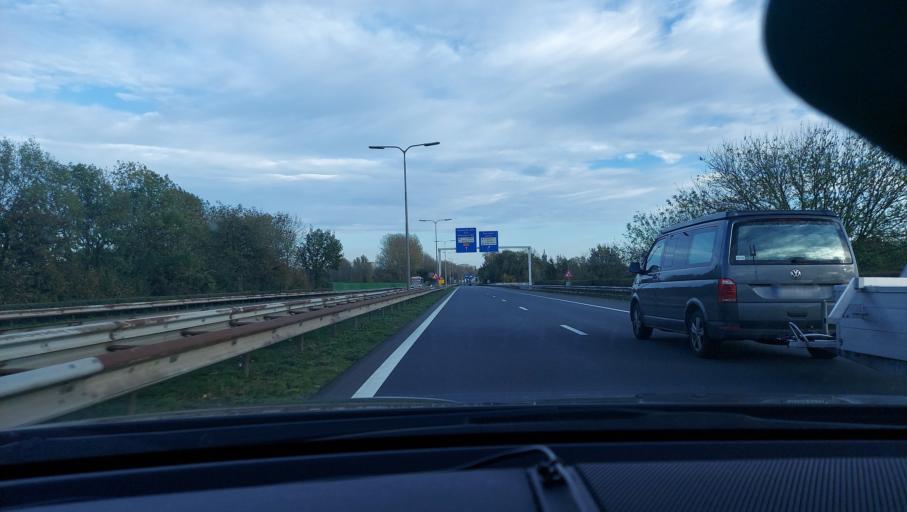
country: NL
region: Limburg
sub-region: Gemeente Roermond
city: Roermond
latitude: 51.2019
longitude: 5.9595
